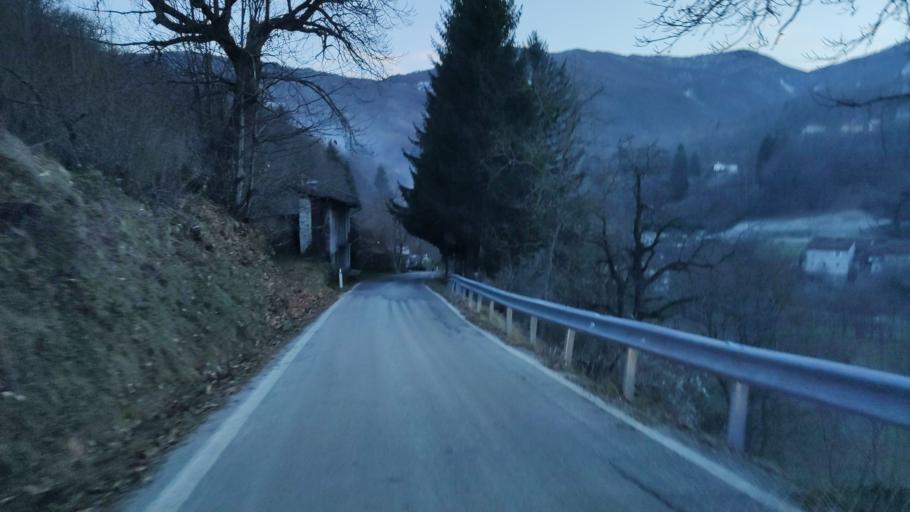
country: IT
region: Piedmont
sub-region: Provincia di Cuneo
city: Viola
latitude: 44.2892
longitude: 7.9780
